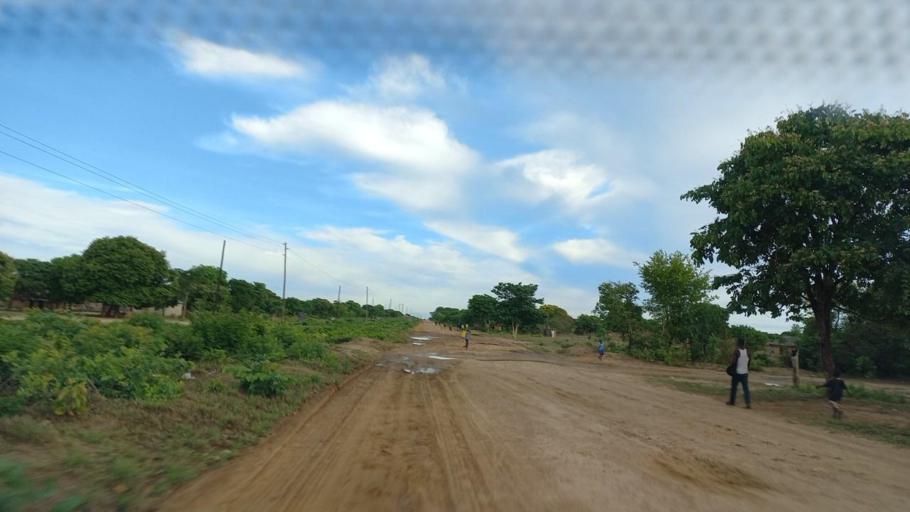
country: ZM
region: North-Western
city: Kabompo
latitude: -13.4248
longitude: 24.3250
